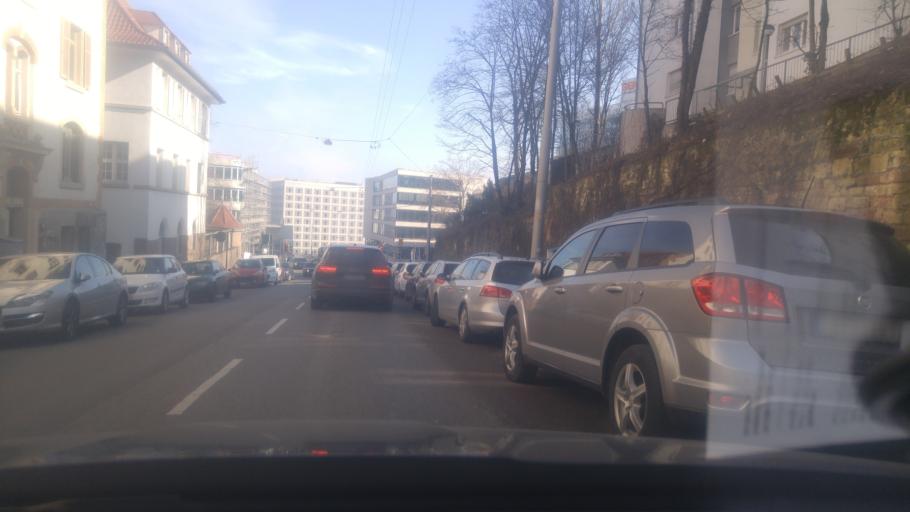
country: DE
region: Baden-Wuerttemberg
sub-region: Regierungsbezirk Stuttgart
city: Stuttgart
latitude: 48.7913
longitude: 9.1779
